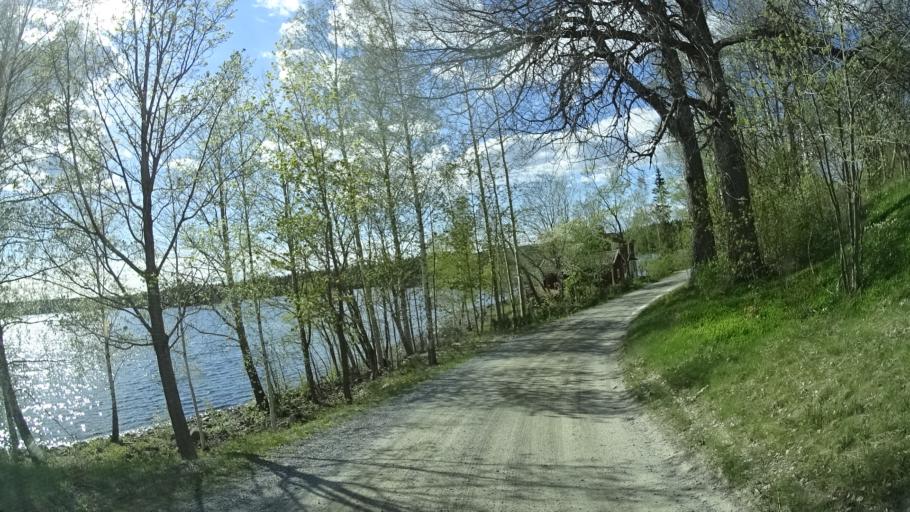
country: SE
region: OErebro
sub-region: Nora Kommun
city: As
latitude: 59.4458
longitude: 14.8118
